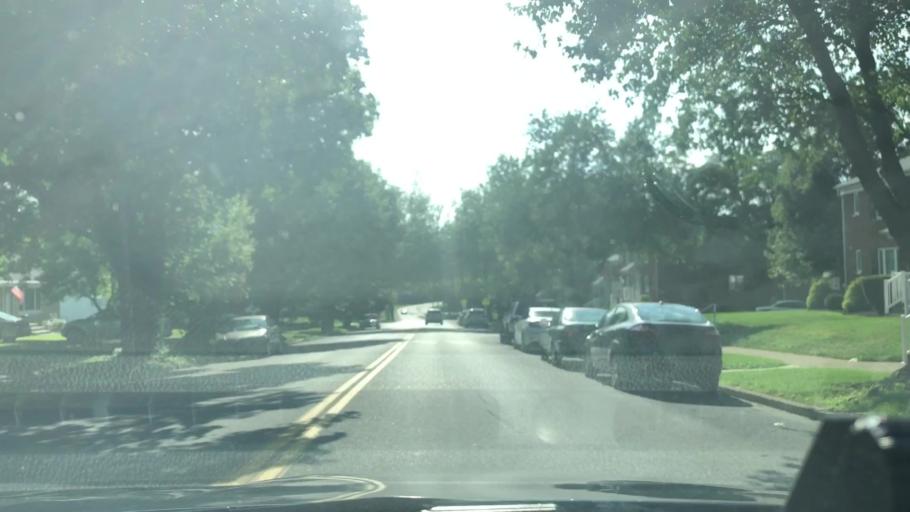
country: US
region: Pennsylvania
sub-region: Northampton County
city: Bethlehem
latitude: 40.6398
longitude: -75.4044
